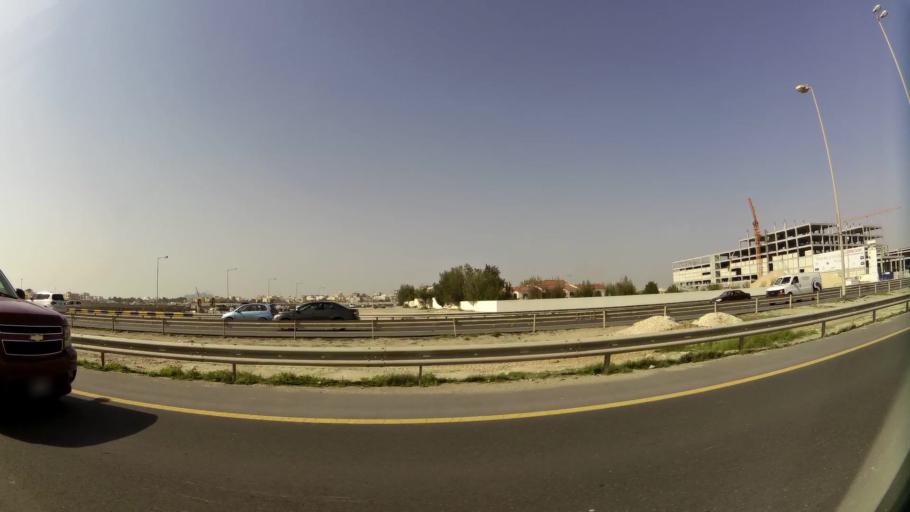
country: BH
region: Central Governorate
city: Madinat Hamad
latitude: 26.1743
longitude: 50.4823
